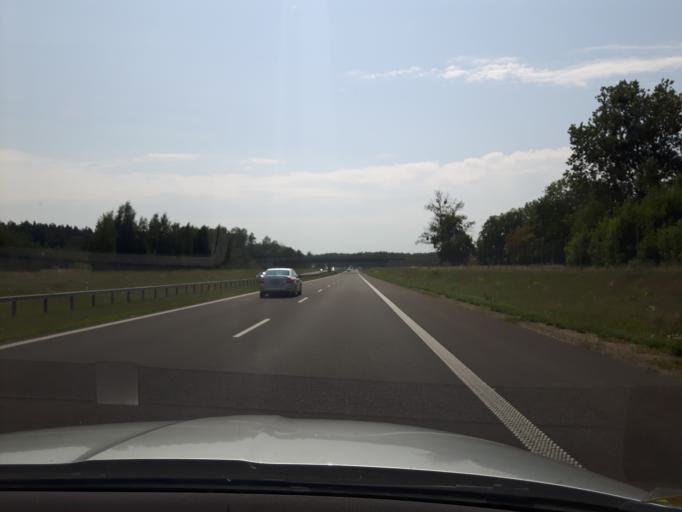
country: PL
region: Masovian Voivodeship
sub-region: Powiat mlawski
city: Wieczfnia Koscielna
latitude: 53.2654
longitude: 20.4299
